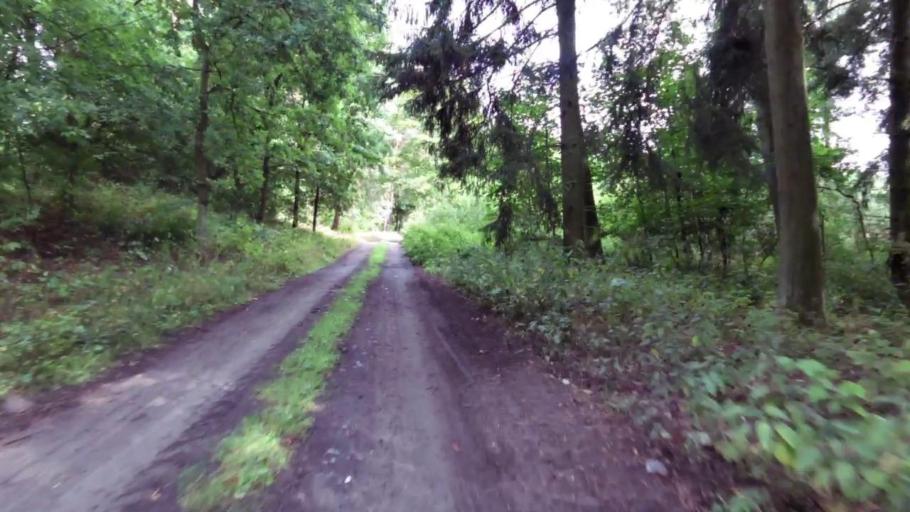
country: PL
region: West Pomeranian Voivodeship
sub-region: Powiat mysliborski
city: Debno
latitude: 52.8163
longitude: 14.6744
